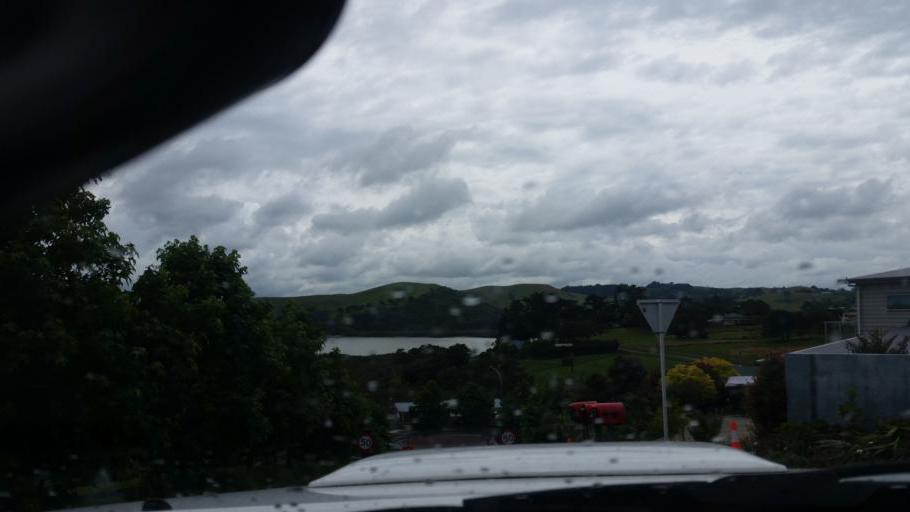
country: NZ
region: Auckland
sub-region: Auckland
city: Wellsford
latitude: -36.1527
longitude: 174.2227
